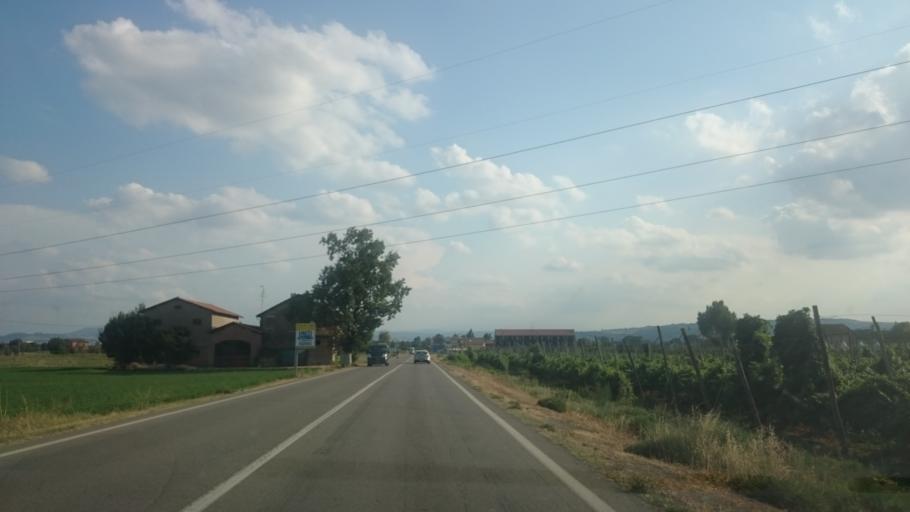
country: IT
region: Emilia-Romagna
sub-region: Provincia di Reggio Emilia
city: Salvaterra
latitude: 44.6108
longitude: 10.7782
